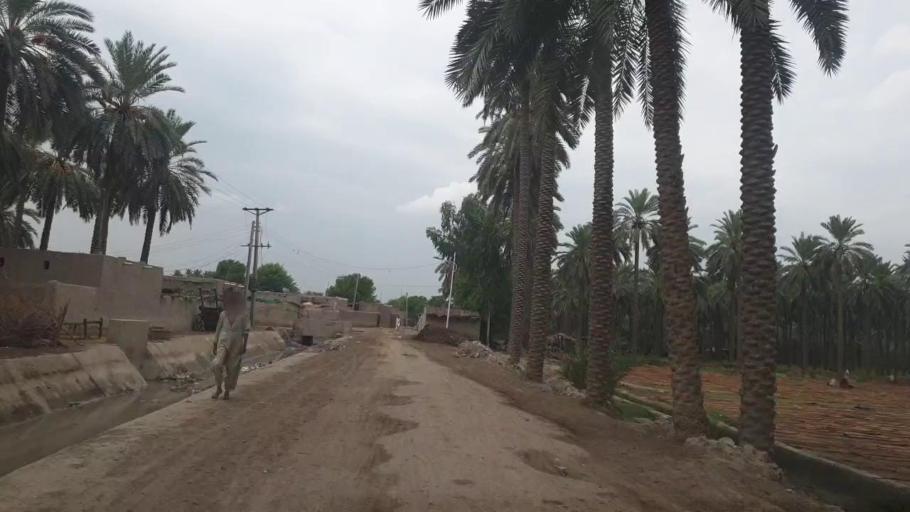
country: PK
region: Sindh
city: Khairpur
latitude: 27.6056
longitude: 68.8032
